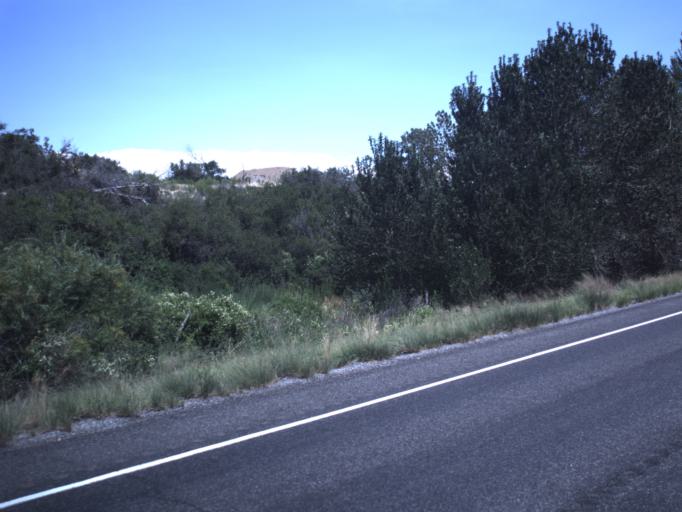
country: US
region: Utah
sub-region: Emery County
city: Huntington
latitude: 39.3536
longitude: -111.0161
